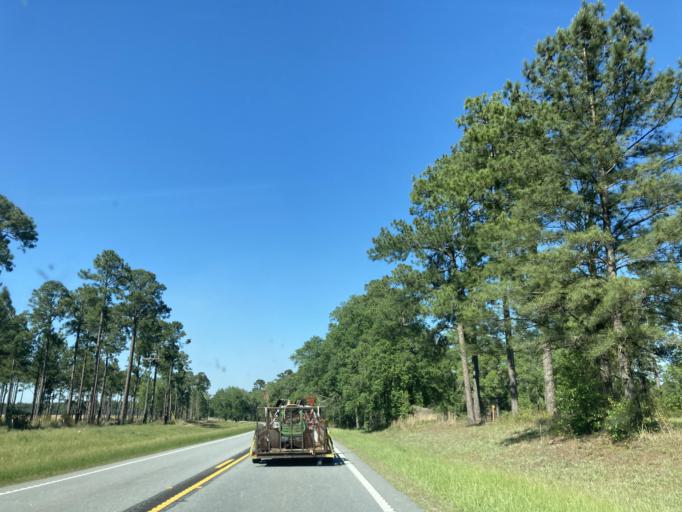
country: US
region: Georgia
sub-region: Baker County
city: Newton
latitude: 31.3702
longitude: -84.2868
